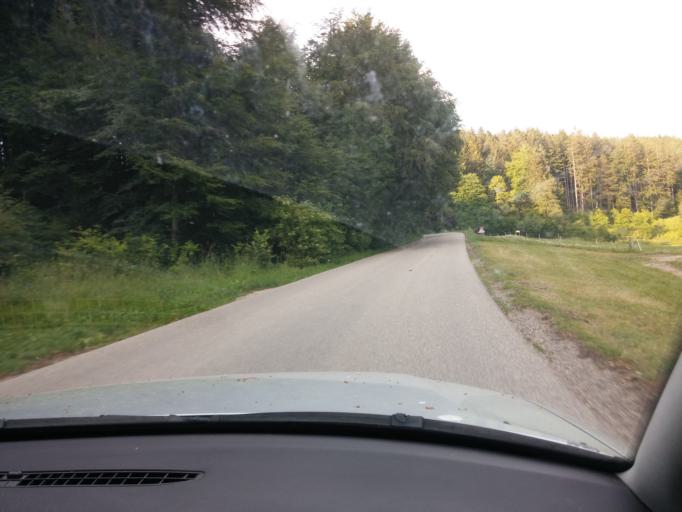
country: DE
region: Bavaria
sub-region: Upper Bavaria
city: Grafing bei Munchen
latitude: 48.0576
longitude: 11.9927
